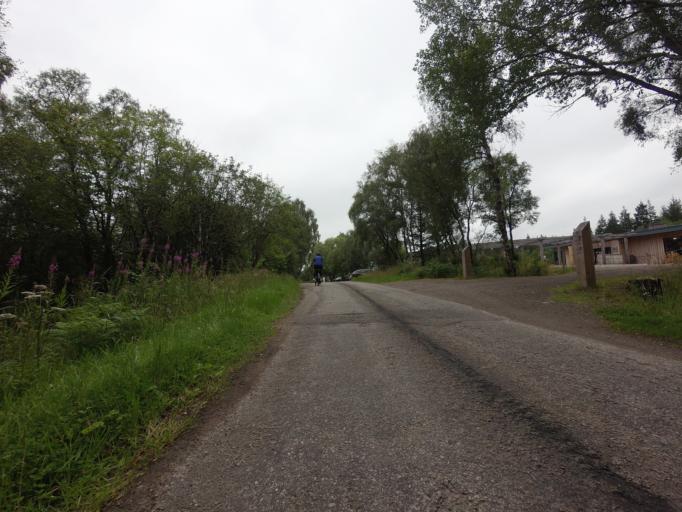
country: GB
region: Scotland
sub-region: Highland
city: Evanton
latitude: 57.9612
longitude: -4.4082
